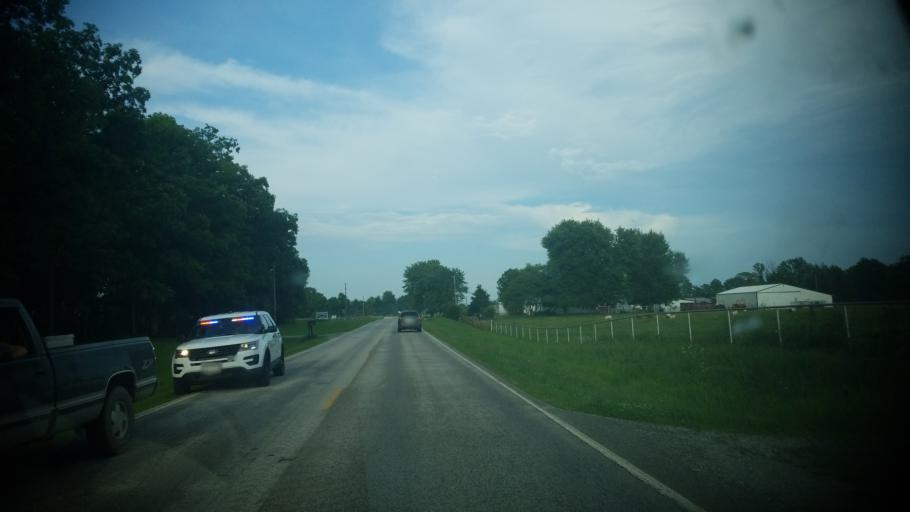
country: US
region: Illinois
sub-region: Clay County
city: Flora
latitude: 38.5168
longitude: -88.4917
